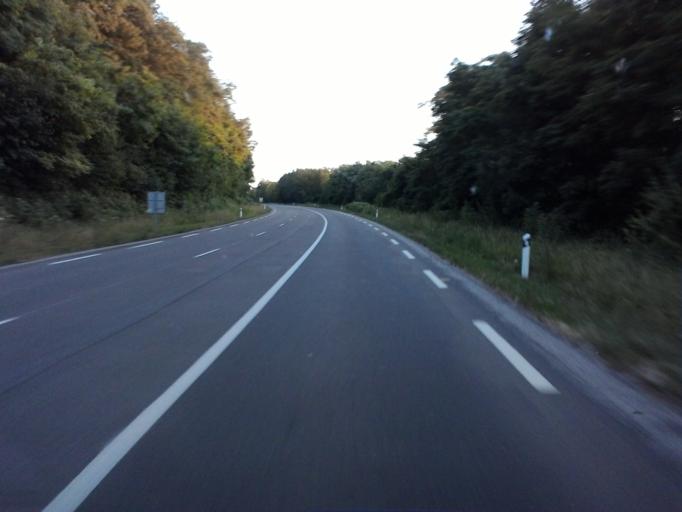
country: FR
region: Franche-Comte
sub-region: Departement du Jura
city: Mouchard
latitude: 46.9654
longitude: 5.7960
